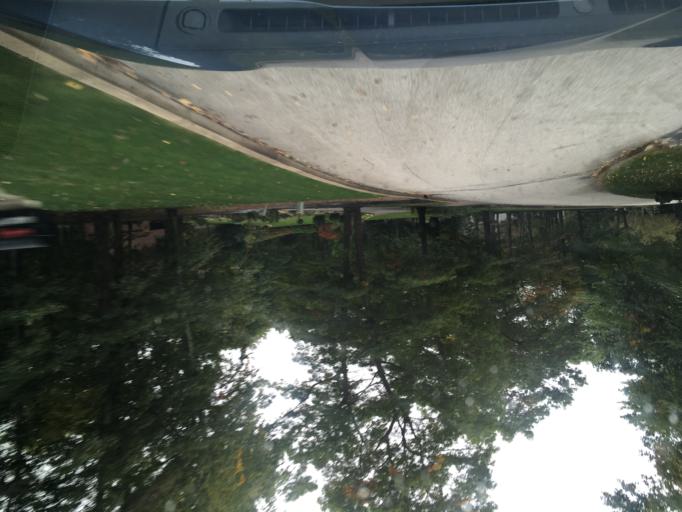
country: US
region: Rhode Island
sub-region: Washington County
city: Exeter
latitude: 41.6115
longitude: -71.5427
